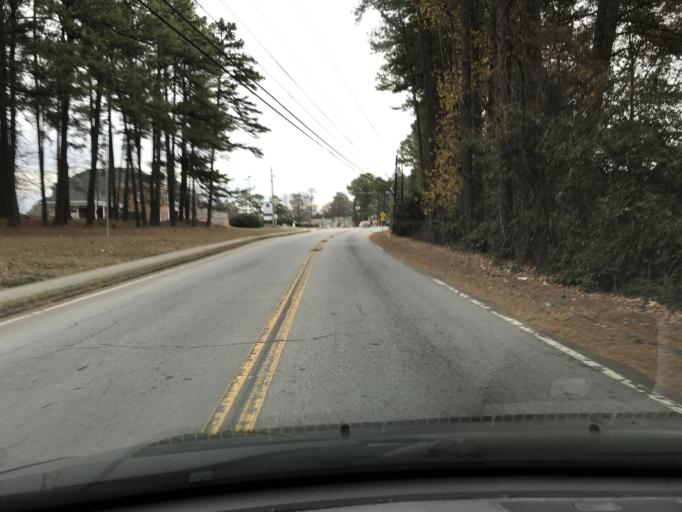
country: US
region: Georgia
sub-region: DeKalb County
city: Tucker
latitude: 33.8810
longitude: -84.2464
